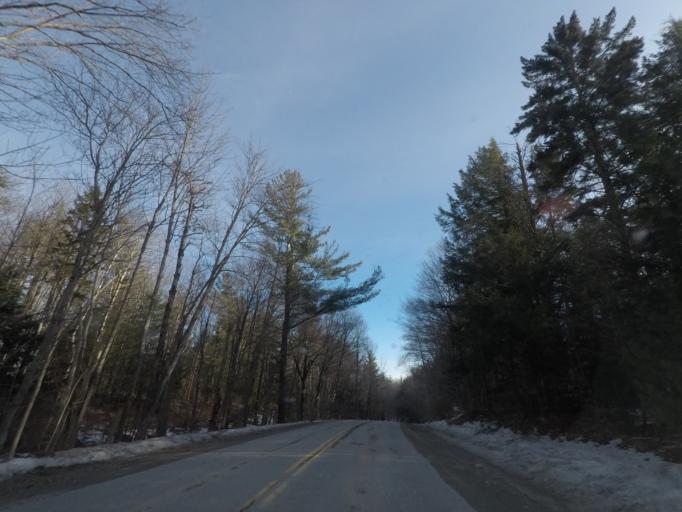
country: US
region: New York
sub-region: Rensselaer County
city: Hoosick Falls
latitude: 42.7431
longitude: -73.4043
